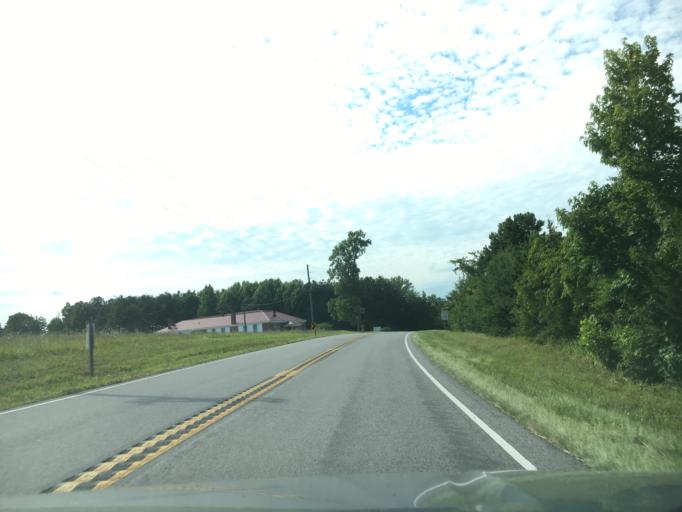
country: US
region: Virginia
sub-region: Halifax County
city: Mountain Road
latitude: 36.8552
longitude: -79.0044
